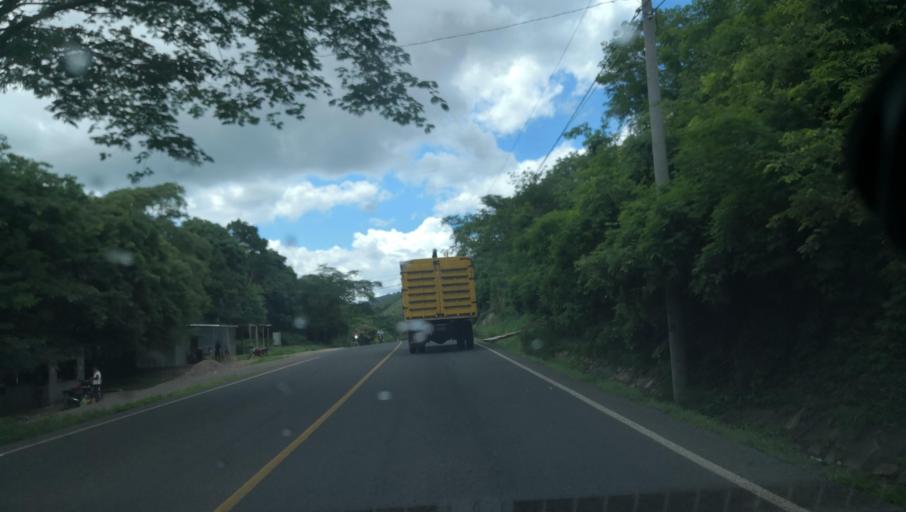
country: NI
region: Madriz
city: Yalaguina
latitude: 13.4601
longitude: -86.4669
